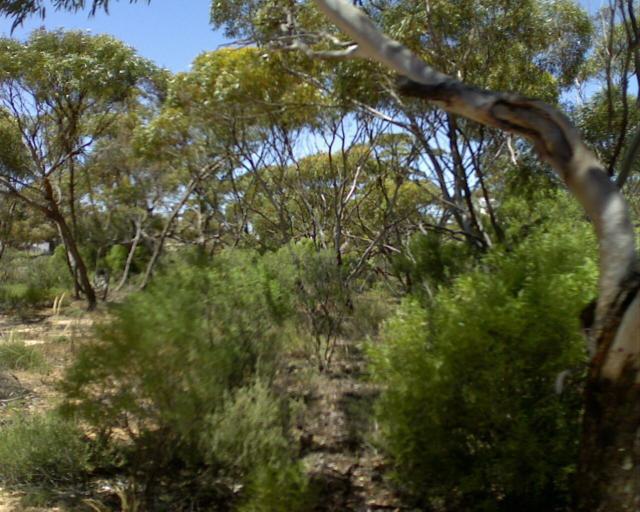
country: AU
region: South Australia
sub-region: Kimba
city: Caralue
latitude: -32.9451
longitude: 135.2744
